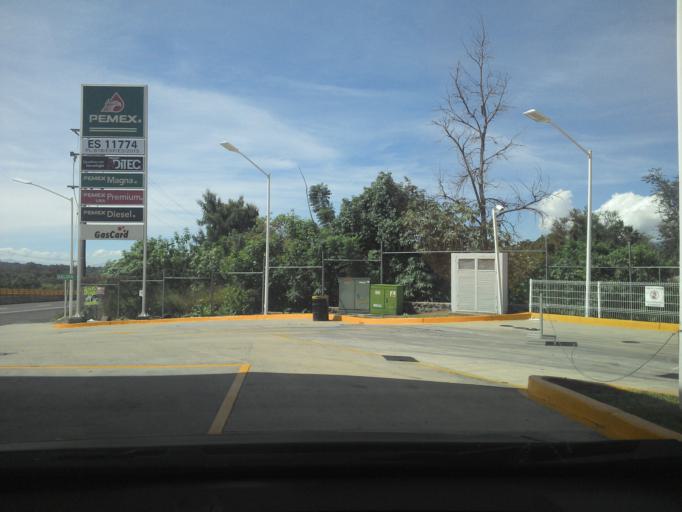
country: MX
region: Jalisco
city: La Venta del Astillero
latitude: 20.7315
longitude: -103.6071
